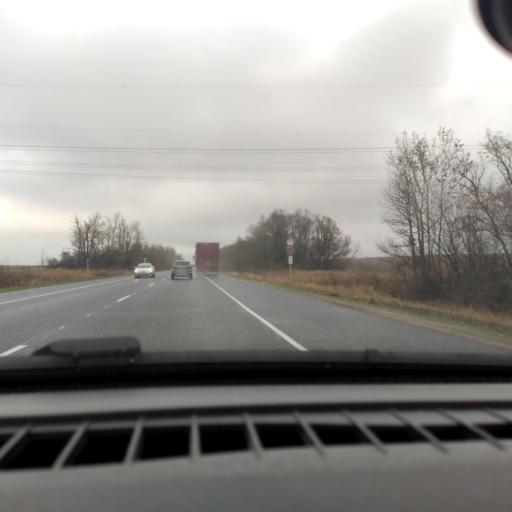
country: RU
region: Voronezj
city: Kolodeznyy
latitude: 51.2416
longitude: 39.0569
